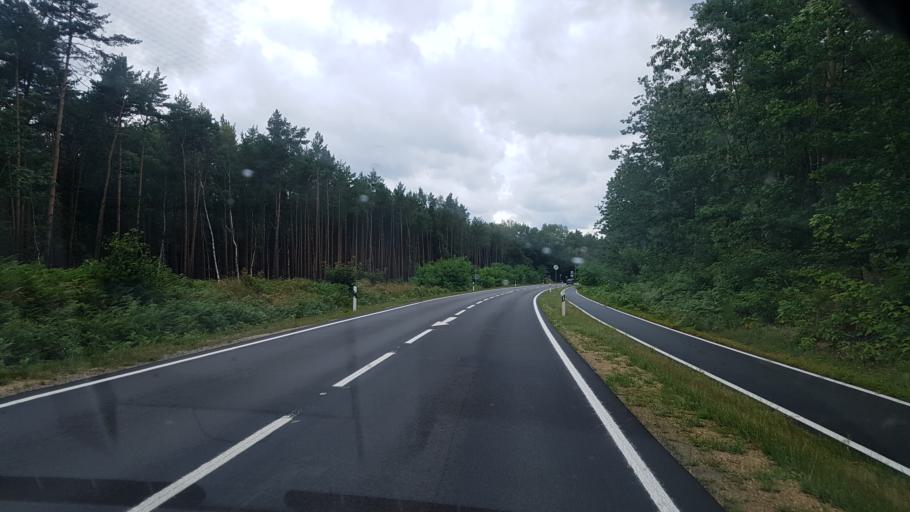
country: DE
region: Saxony
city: Niesky
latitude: 51.2966
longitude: 14.8088
